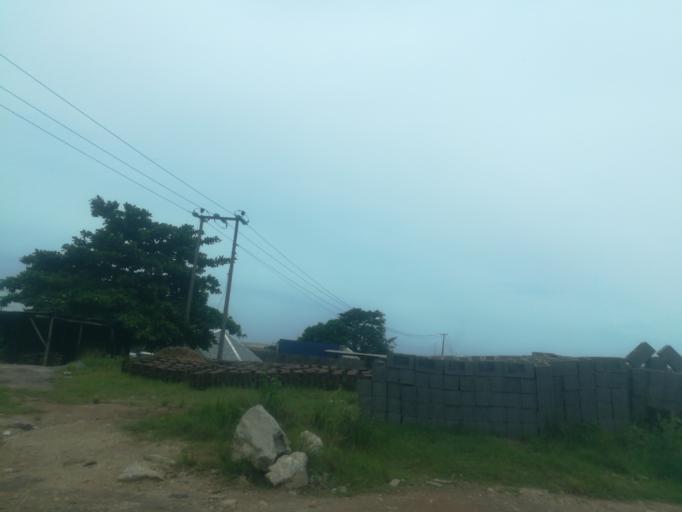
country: NG
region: Oyo
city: Ibadan
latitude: 7.3338
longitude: 3.8870
